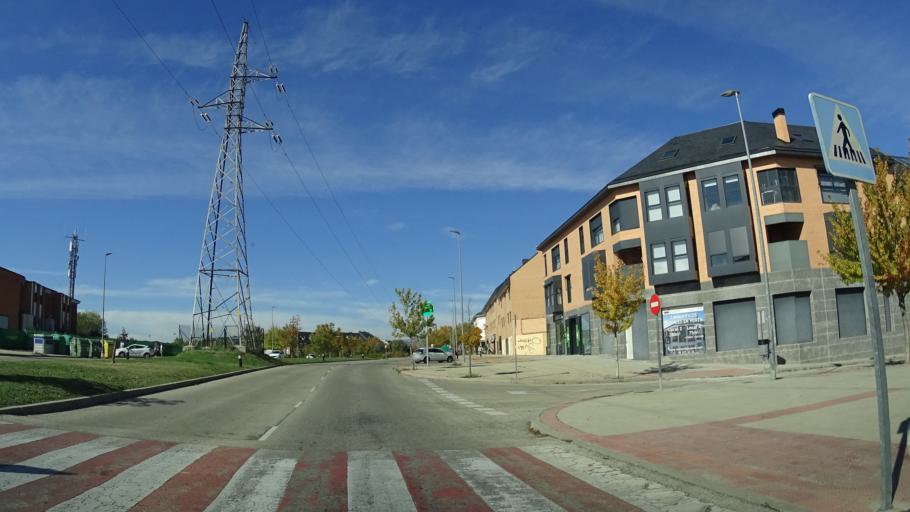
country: ES
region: Madrid
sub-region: Provincia de Madrid
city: Villanueva del Pardillo
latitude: 40.4936
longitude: -3.9607
